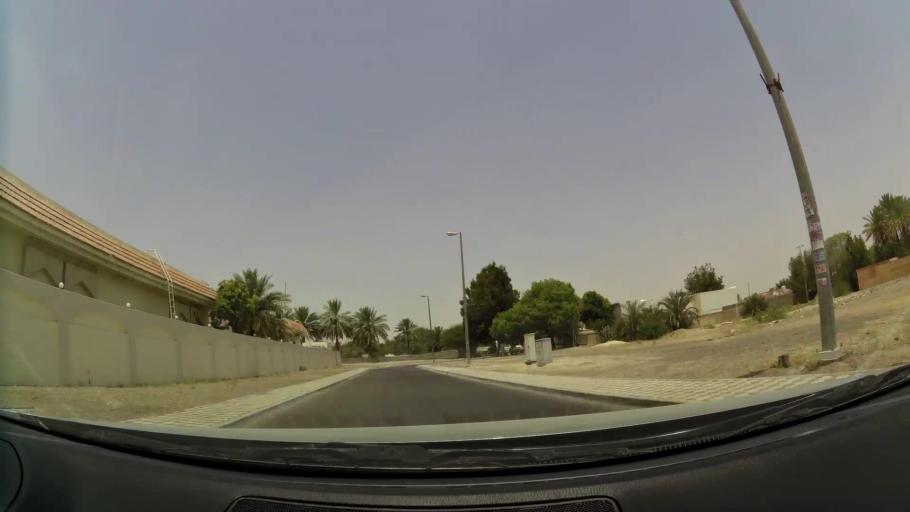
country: AE
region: Abu Dhabi
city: Al Ain
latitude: 24.2014
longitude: 55.7801
